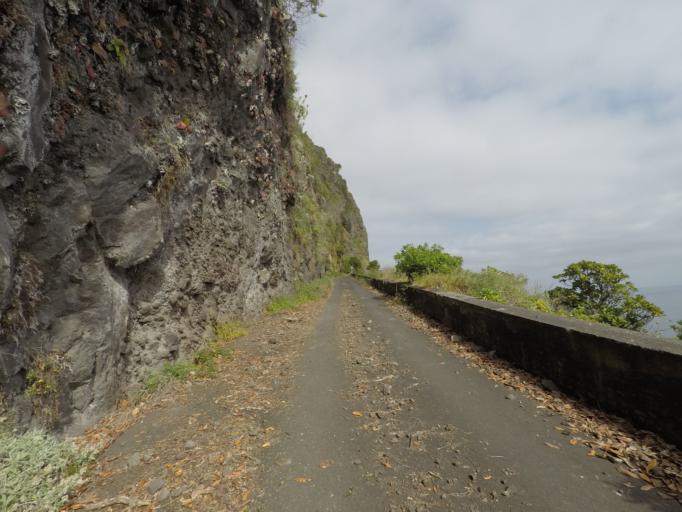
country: PT
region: Madeira
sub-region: Sao Vicente
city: Sao Vicente
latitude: 32.8113
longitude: -17.0632
